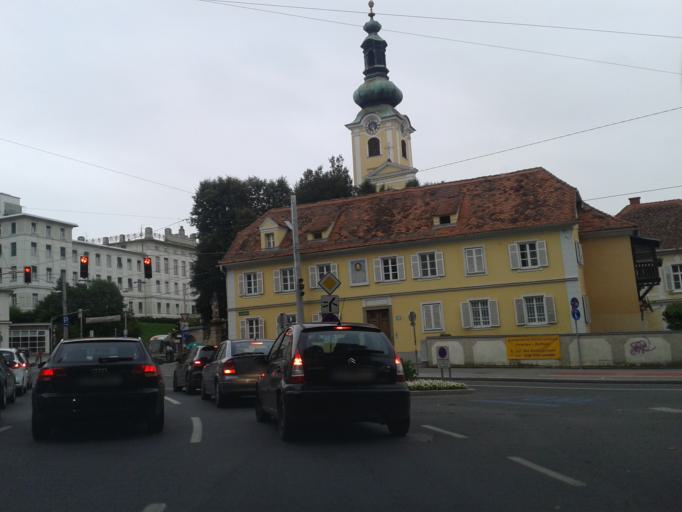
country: AT
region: Styria
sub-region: Graz Stadt
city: Graz
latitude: 47.0783
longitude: 15.4639
